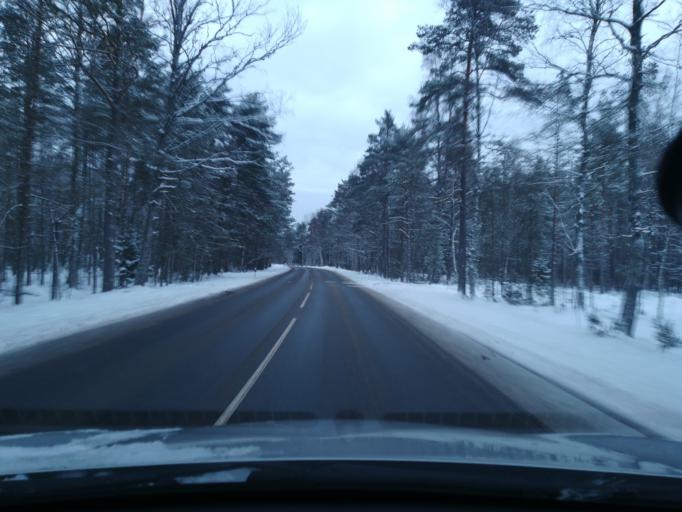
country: EE
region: Harju
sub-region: Paldiski linn
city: Paldiski
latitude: 59.3895
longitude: 24.2411
